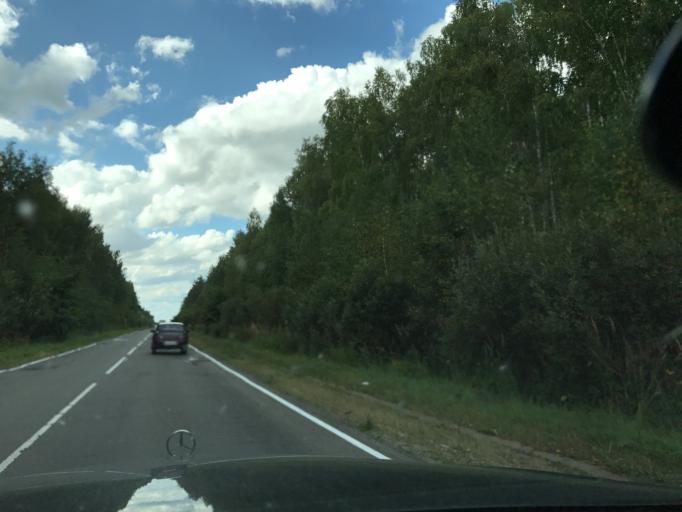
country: RU
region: Vladimir
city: Raduzhnyy
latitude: 55.9858
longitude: 40.2347
